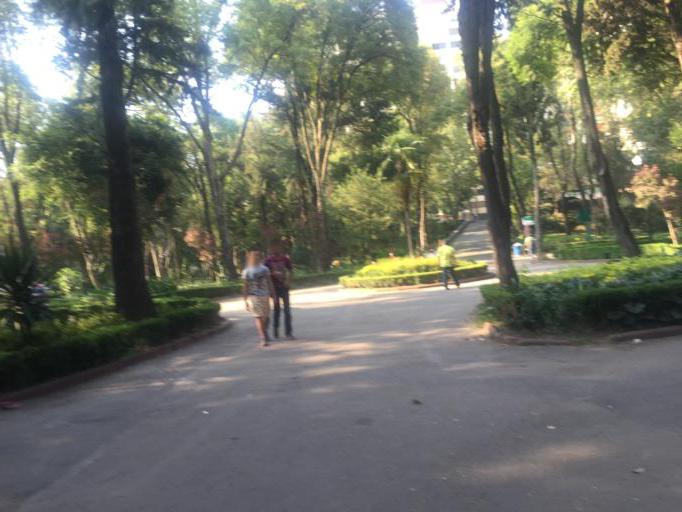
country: MX
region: Mexico City
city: Colonia del Valle
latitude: 19.3779
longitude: -99.1803
